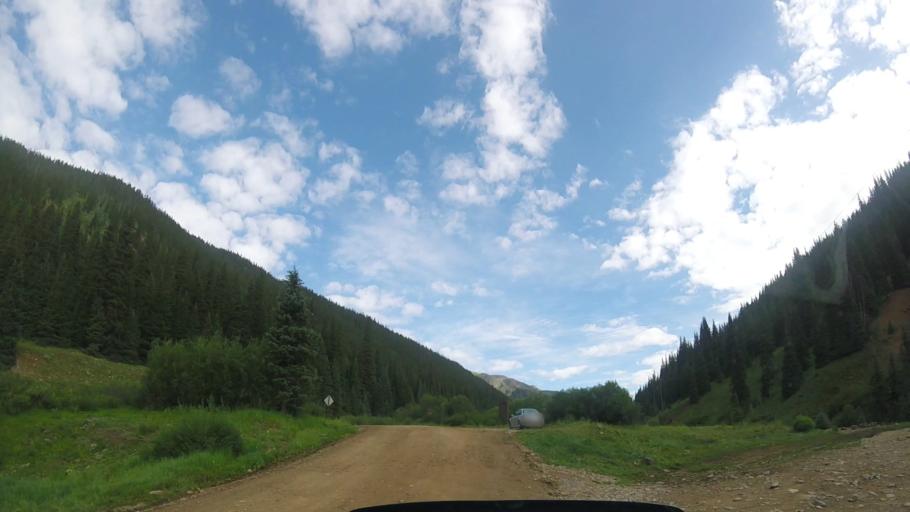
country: US
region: Colorado
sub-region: San Juan County
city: Silverton
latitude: 37.8510
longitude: -107.7263
